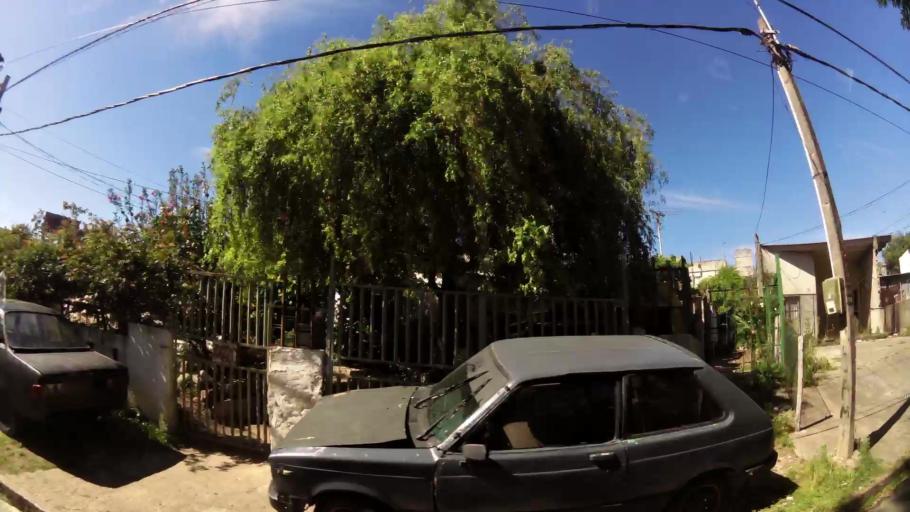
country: UY
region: Montevideo
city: Montevideo
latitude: -34.8877
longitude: -56.1349
